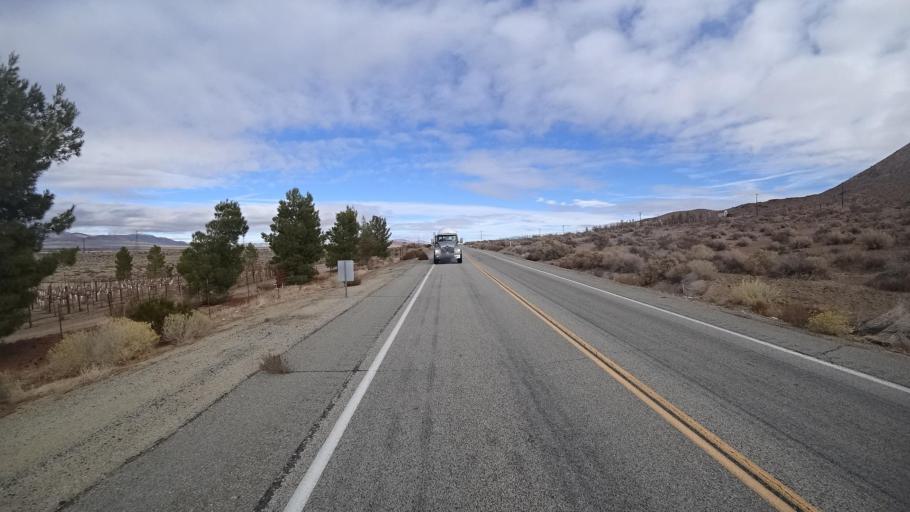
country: US
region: California
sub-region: Kern County
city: Rosamond
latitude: 34.8811
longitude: -118.2934
